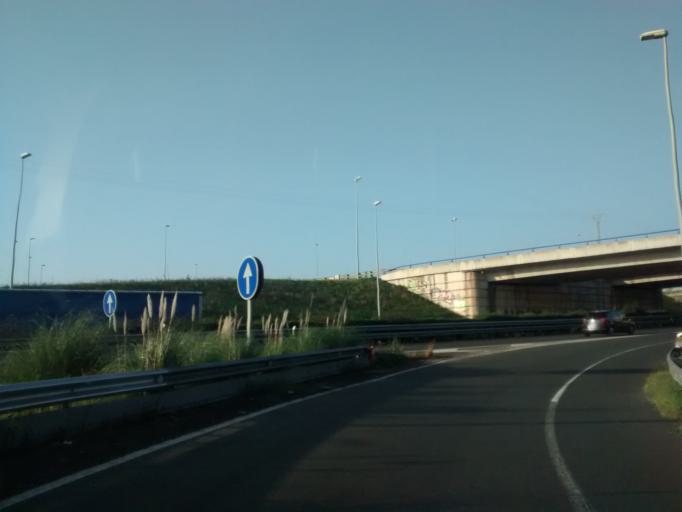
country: ES
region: Cantabria
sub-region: Provincia de Cantabria
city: Santa Cruz de Bezana
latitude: 43.4367
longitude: -3.8750
